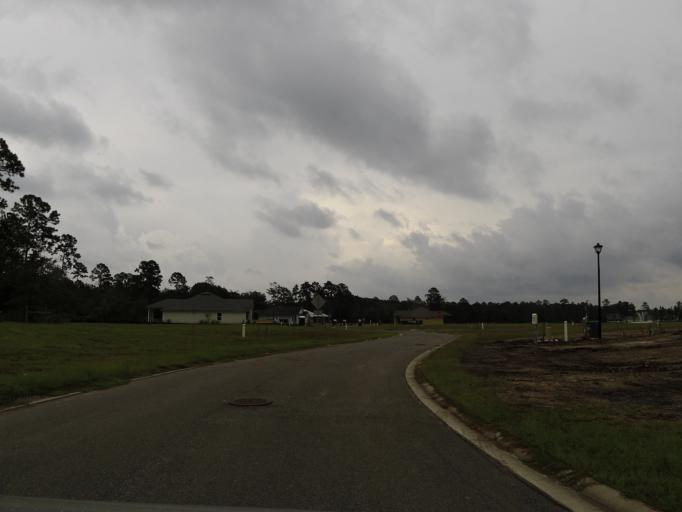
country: US
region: Florida
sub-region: Clay County
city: Middleburg
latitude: 30.1099
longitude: -81.8590
